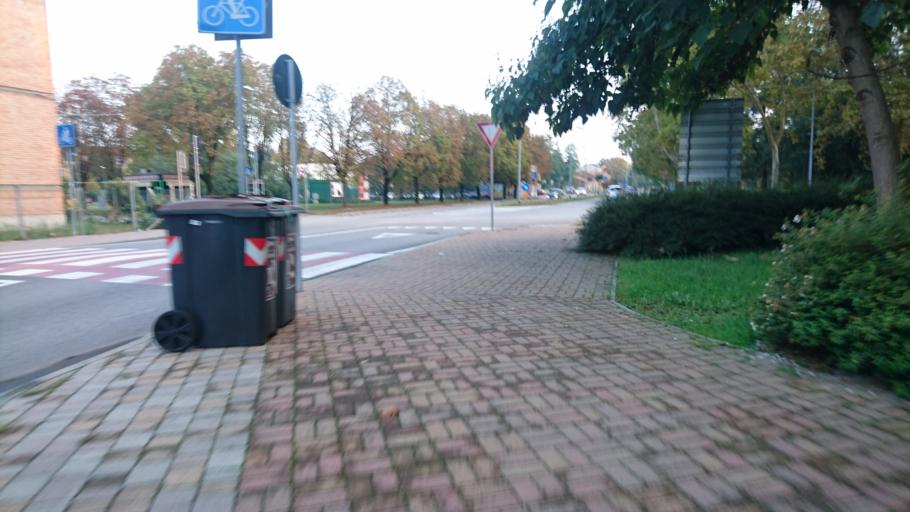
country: IT
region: Emilia-Romagna
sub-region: Provincia di Ferrara
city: Ferrara
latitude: 44.8615
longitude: 11.6072
